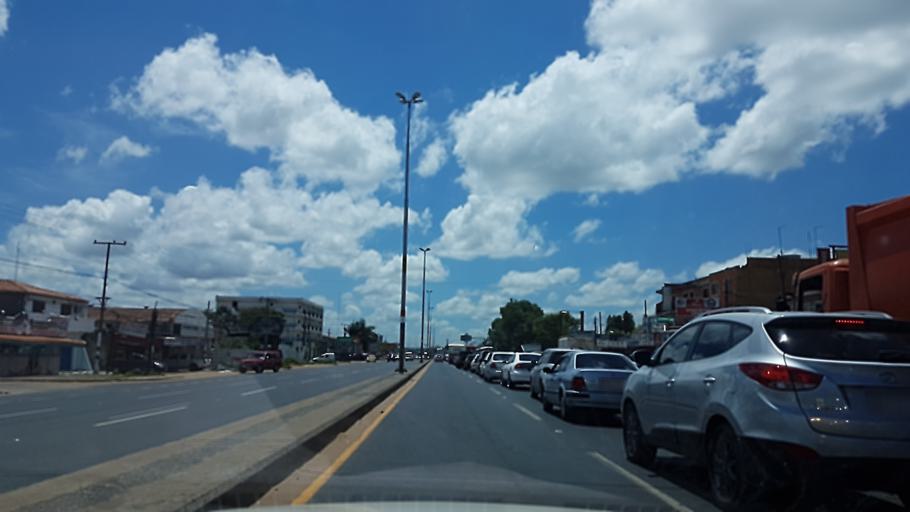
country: PY
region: Central
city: Colonia Mariano Roque Alonso
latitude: -25.2163
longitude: -57.5304
